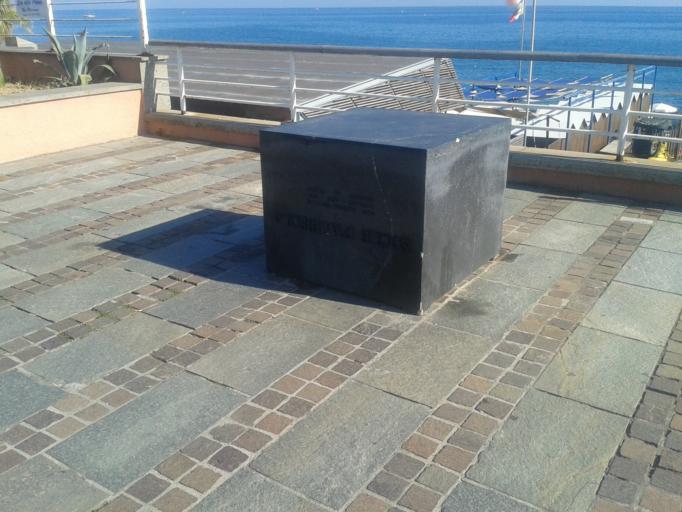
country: IT
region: Liguria
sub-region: Provincia di Savona
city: Albisola Marina
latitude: 44.3298
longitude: 8.5166
